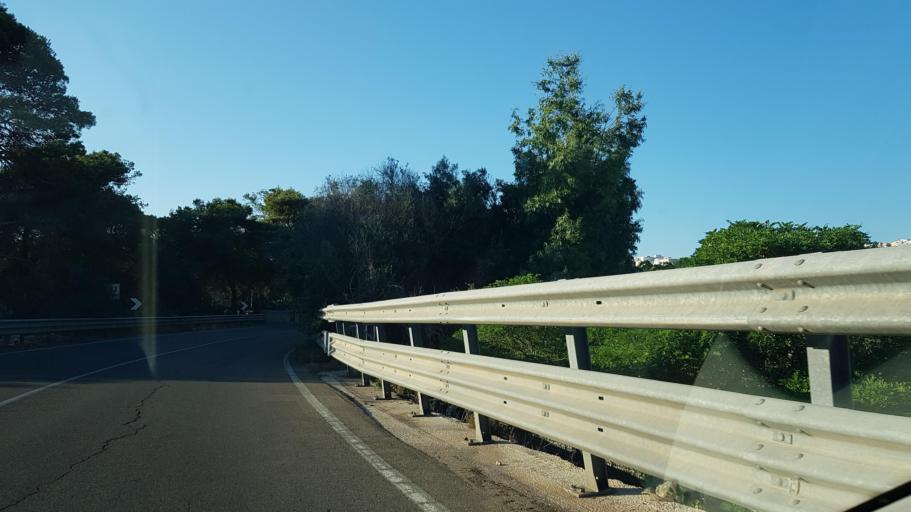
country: IT
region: Apulia
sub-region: Provincia di Lecce
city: Castro
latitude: 40.0012
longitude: 18.4214
